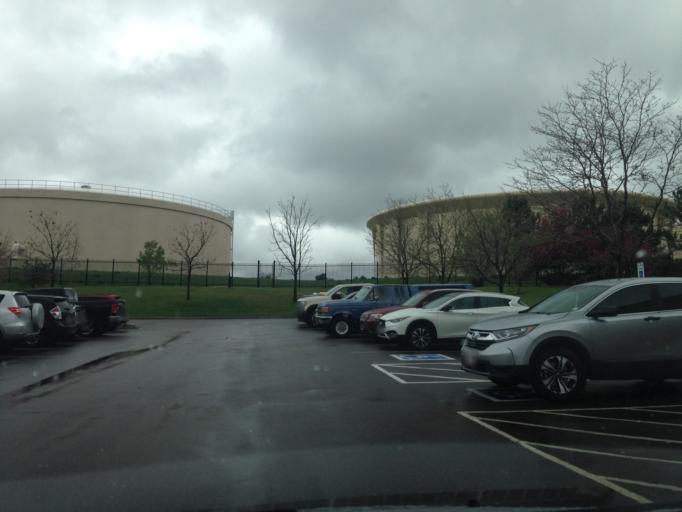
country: US
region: Colorado
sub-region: Adams County
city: Westminster
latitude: 39.8615
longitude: -105.0479
